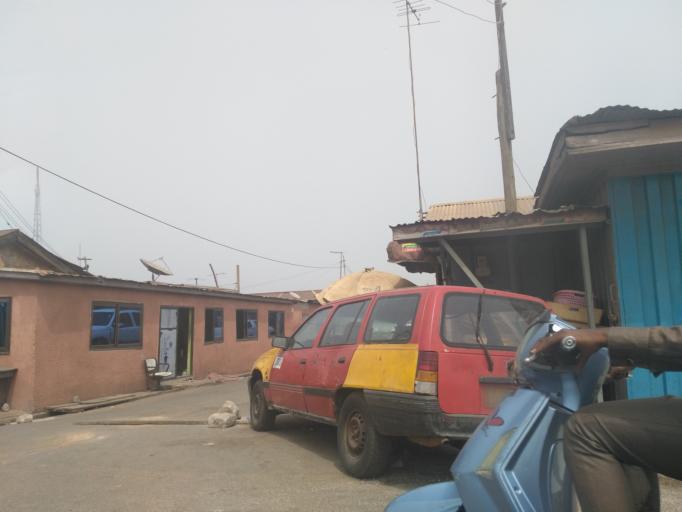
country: GH
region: Ashanti
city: Kumasi
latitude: 6.7014
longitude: -1.6094
